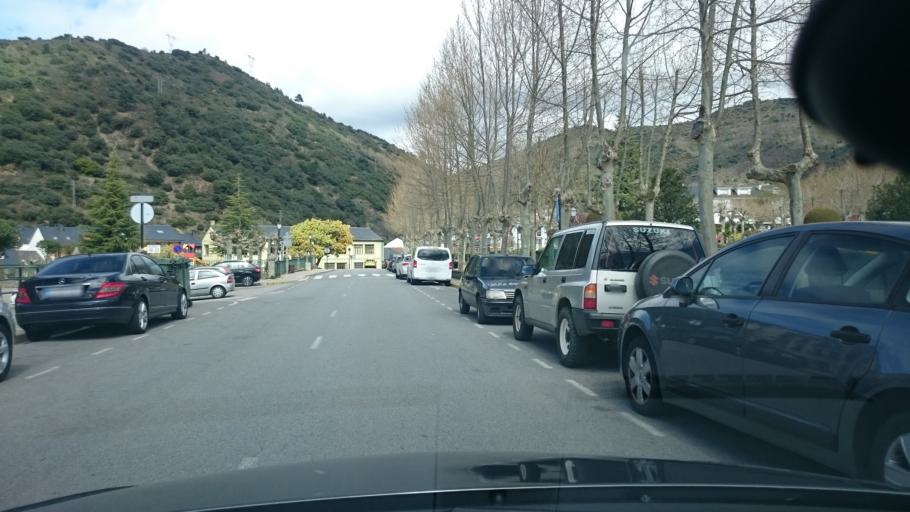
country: ES
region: Castille and Leon
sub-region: Provincia de Leon
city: Villafranca del Bierzo
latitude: 42.6087
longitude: -6.8086
